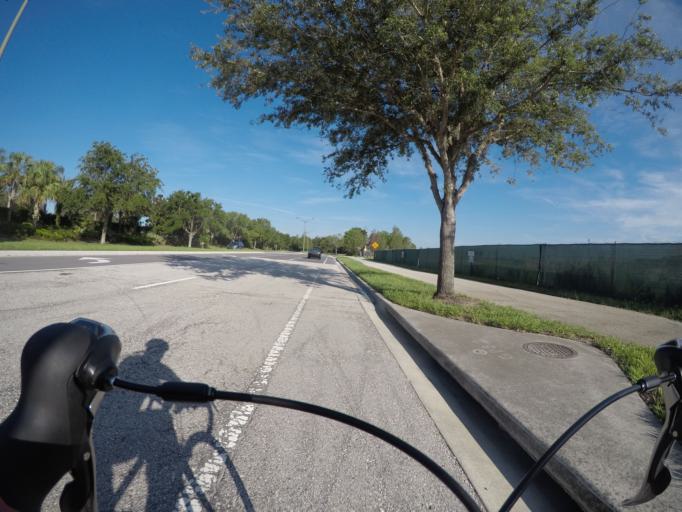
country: US
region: Florida
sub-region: Orange County
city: Meadow Woods
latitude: 28.3972
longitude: -81.2644
